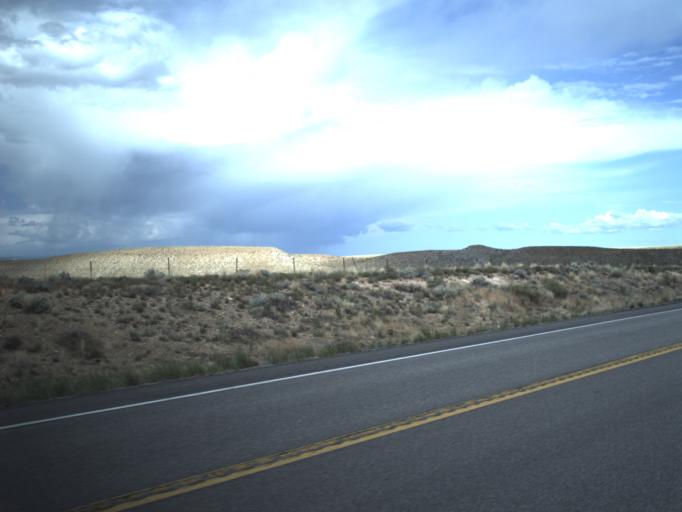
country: US
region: Utah
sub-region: Carbon County
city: East Carbon City
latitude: 39.4965
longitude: -110.5238
